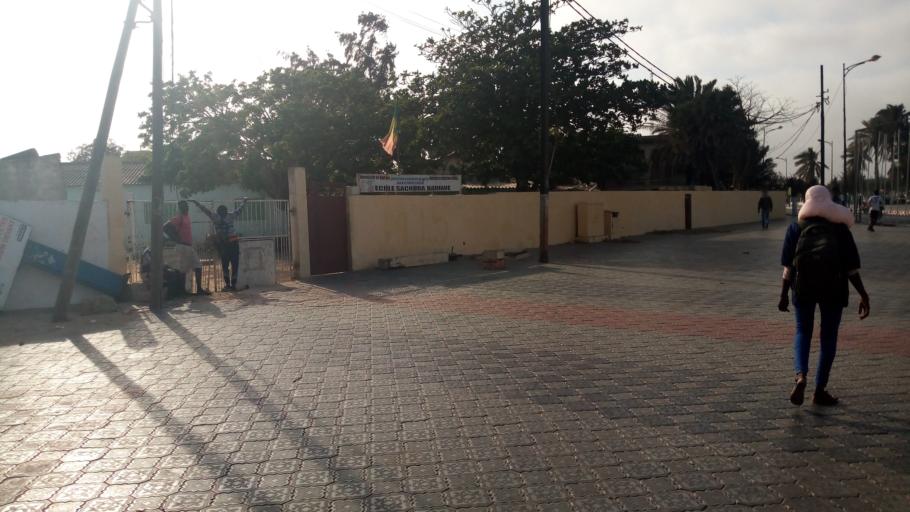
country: SN
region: Dakar
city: Dakar
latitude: 14.6923
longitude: -17.4477
